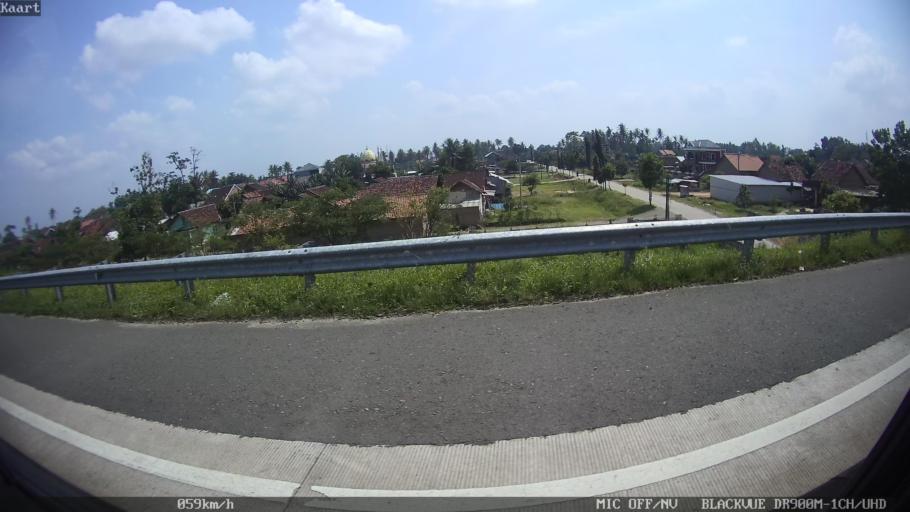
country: ID
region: Lampung
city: Kedaton
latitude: -5.3268
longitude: 105.2826
